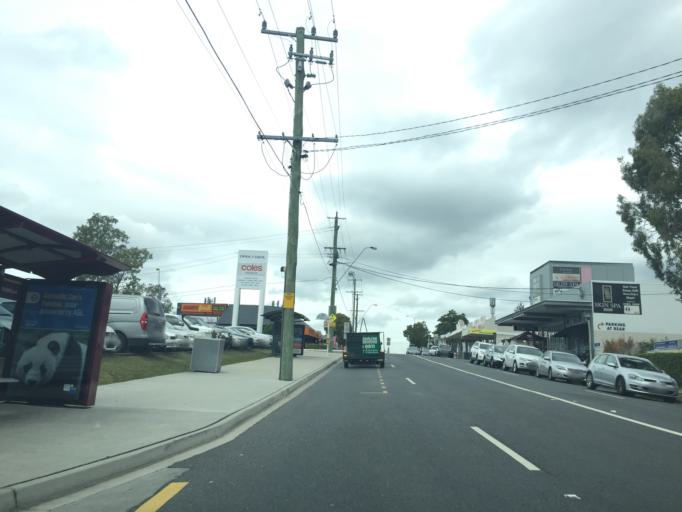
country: AU
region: Queensland
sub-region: Brisbane
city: Milton
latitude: -27.4442
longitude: 152.9914
